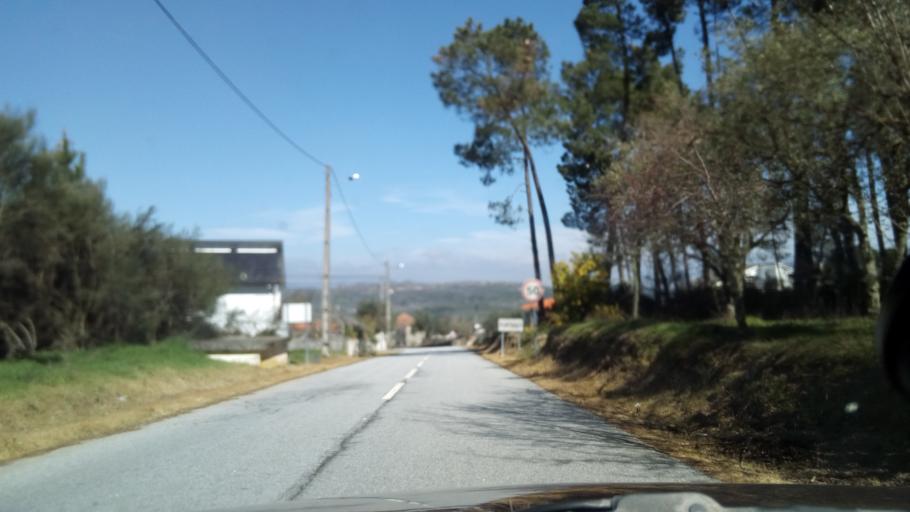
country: PT
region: Guarda
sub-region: Fornos de Algodres
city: Fornos de Algodres
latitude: 40.6532
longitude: -7.5333
